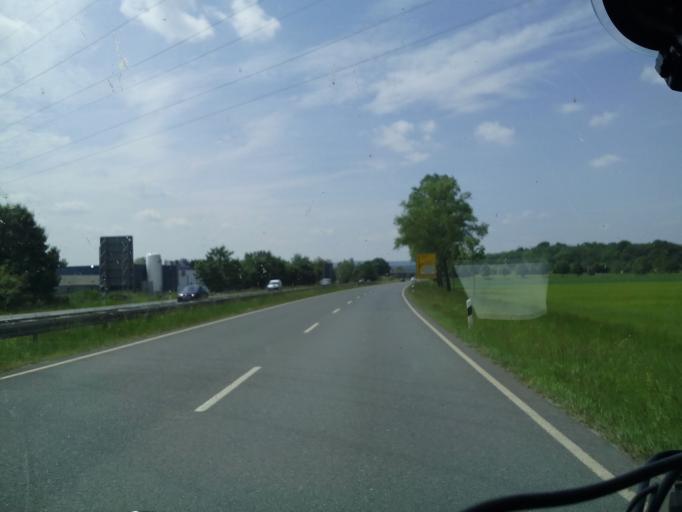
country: DE
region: Bavaria
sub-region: Upper Franconia
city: Kulmbach
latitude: 50.1065
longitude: 11.4268
